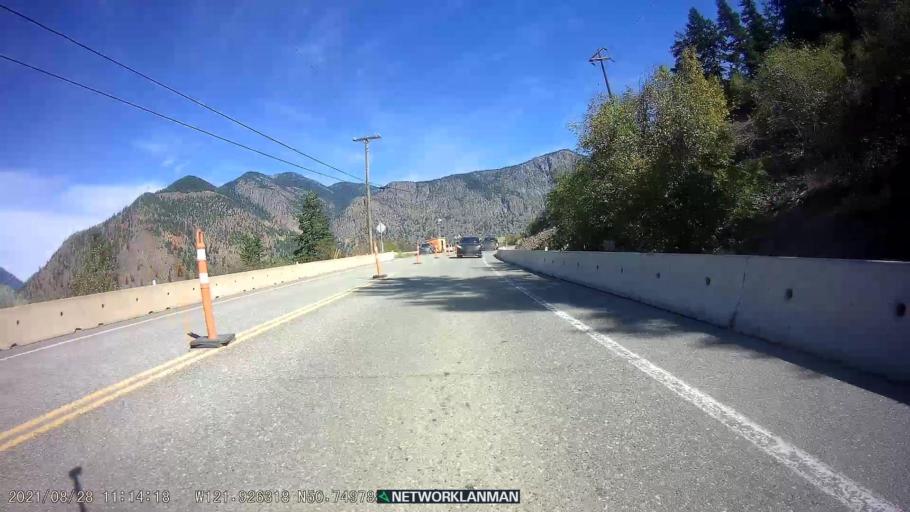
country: CA
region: British Columbia
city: Lillooet
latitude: 50.7501
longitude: -121.9248
